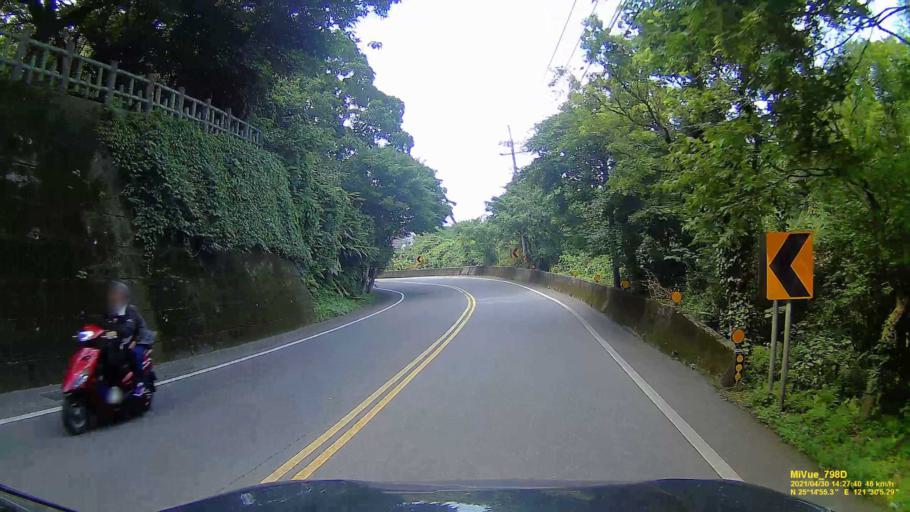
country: TW
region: Taipei
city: Taipei
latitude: 25.2489
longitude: 121.5015
